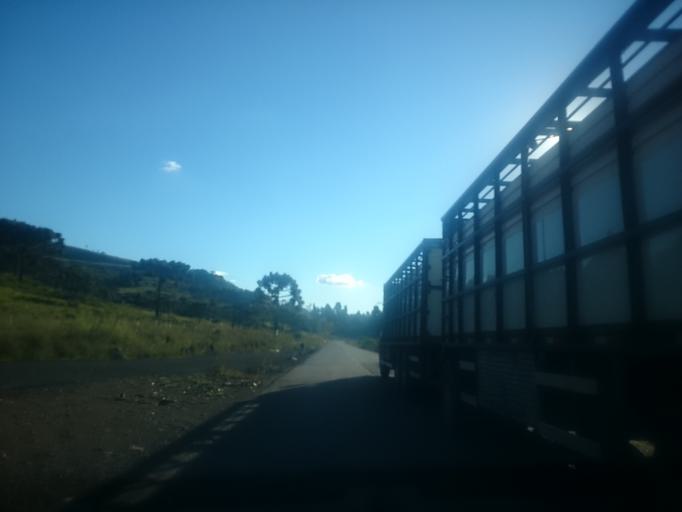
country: BR
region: Santa Catarina
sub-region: Sao Joaquim
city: Sao Joaquim
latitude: -28.2018
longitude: -49.9894
